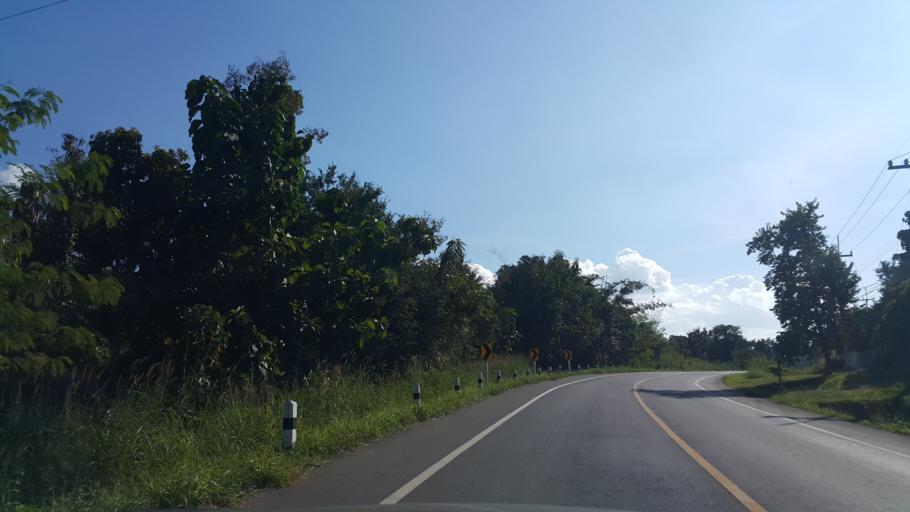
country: TH
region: Lamphun
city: Mae Tha
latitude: 18.4890
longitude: 99.1832
